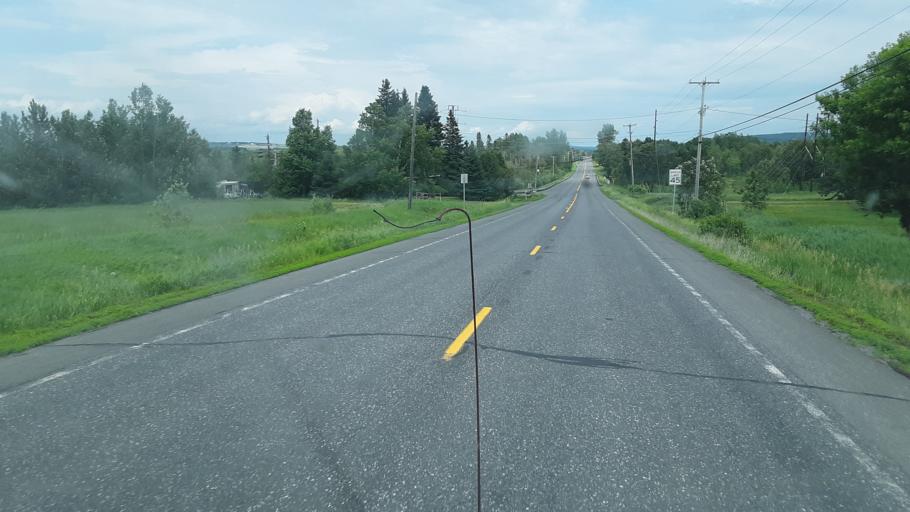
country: US
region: Maine
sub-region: Aroostook County
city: Fort Fairfield
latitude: 46.7592
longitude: -67.8603
